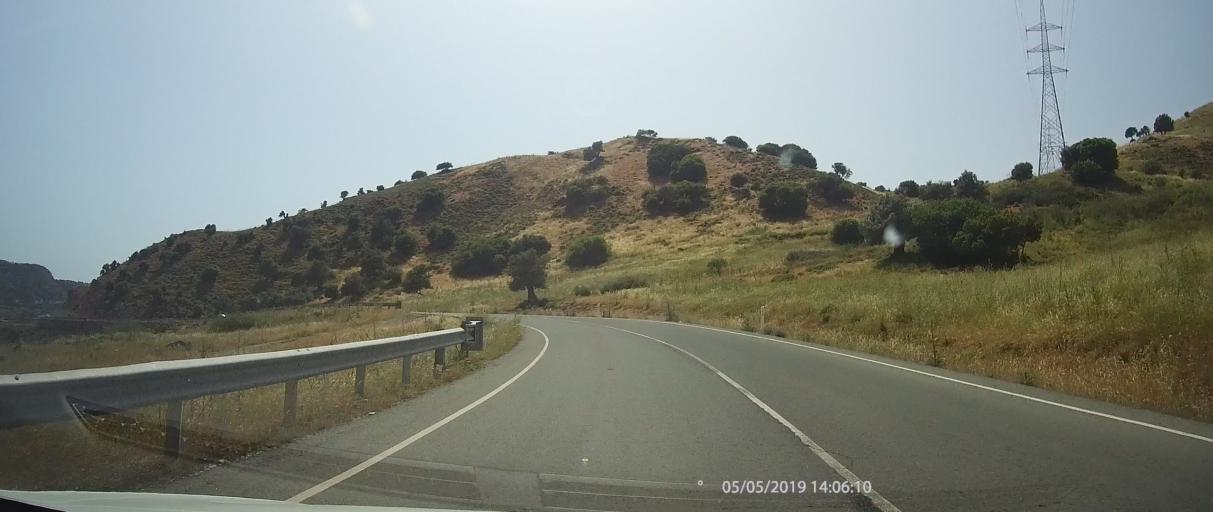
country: CY
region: Limassol
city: Pissouri
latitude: 34.7464
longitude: 32.6080
